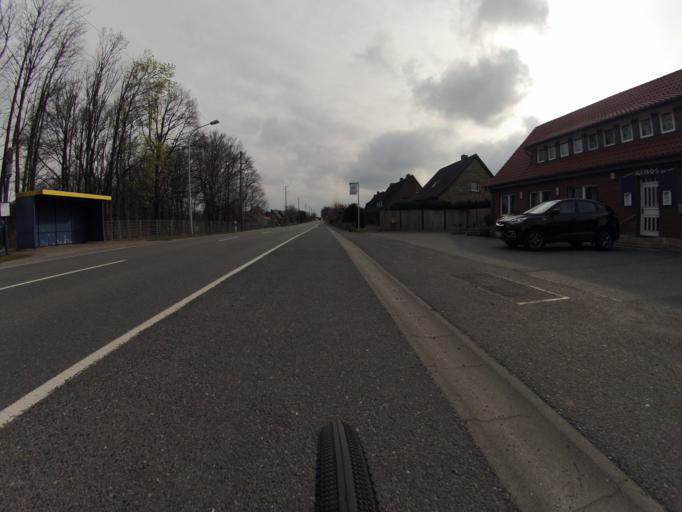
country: DE
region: North Rhine-Westphalia
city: Ibbenburen
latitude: 52.3084
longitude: 7.6936
